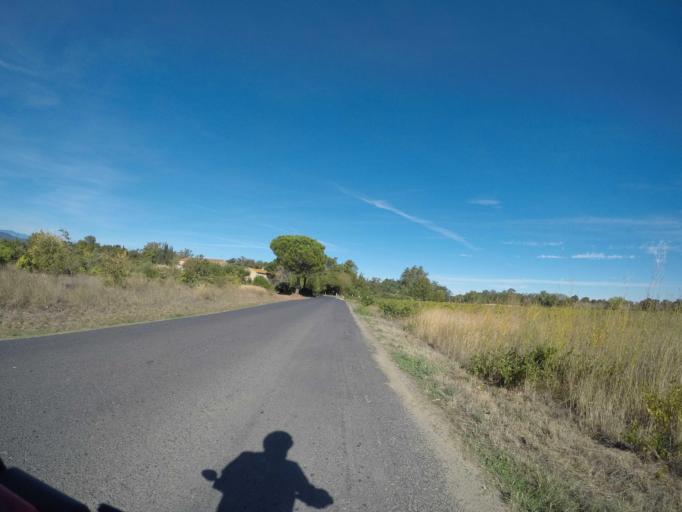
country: FR
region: Languedoc-Roussillon
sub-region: Departement des Pyrenees-Orientales
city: Ponteilla
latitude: 42.6493
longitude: 2.7985
